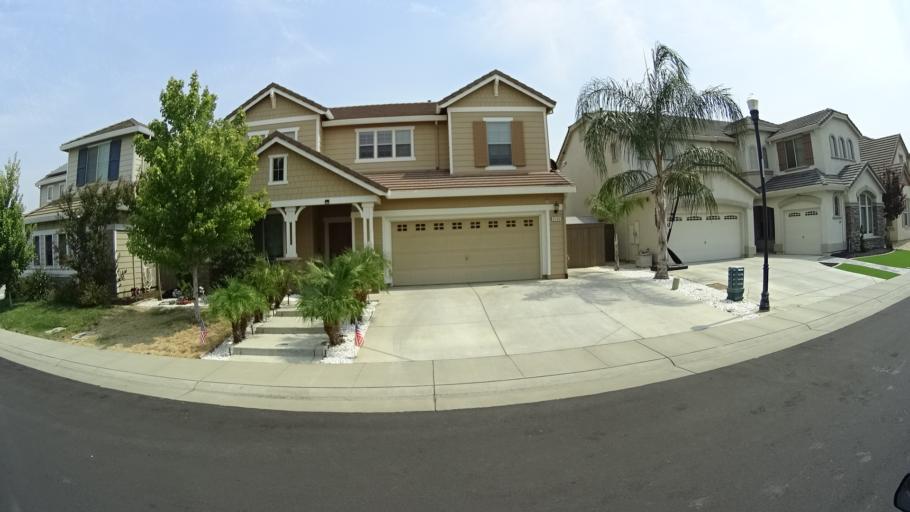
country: US
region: California
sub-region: Sacramento County
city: Laguna
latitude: 38.4038
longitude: -121.4160
